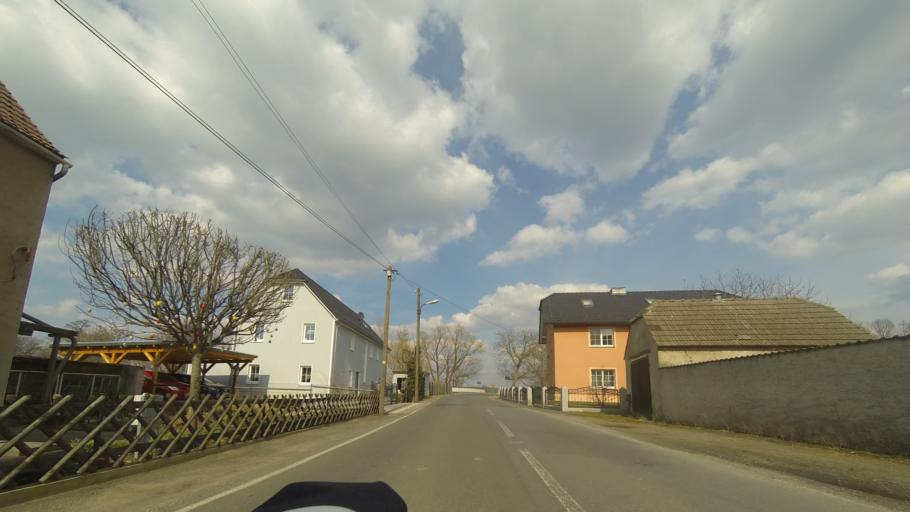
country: DE
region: Saxony
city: Ebersbach
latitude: 51.2608
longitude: 13.6786
